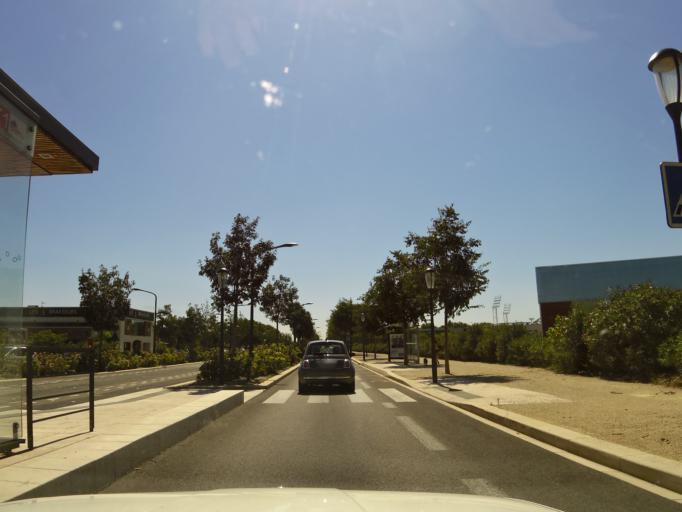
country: FR
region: Languedoc-Roussillon
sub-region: Departement du Gard
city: Nimes
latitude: 43.8195
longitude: 4.3586
